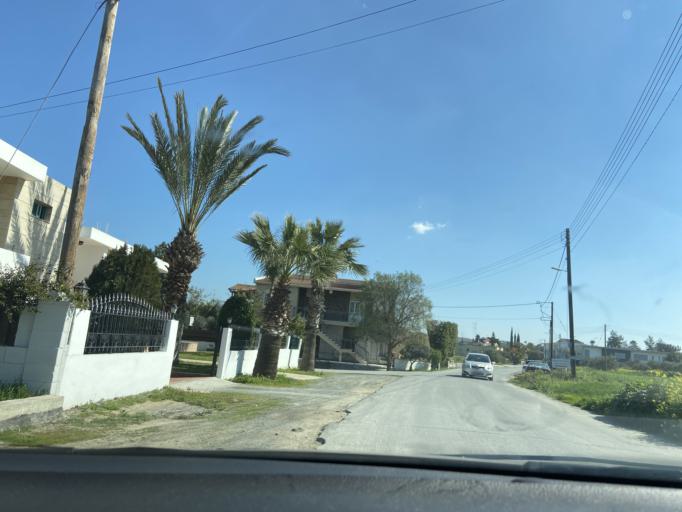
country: CY
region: Lefkosia
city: Dali
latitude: 35.0168
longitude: 33.4096
